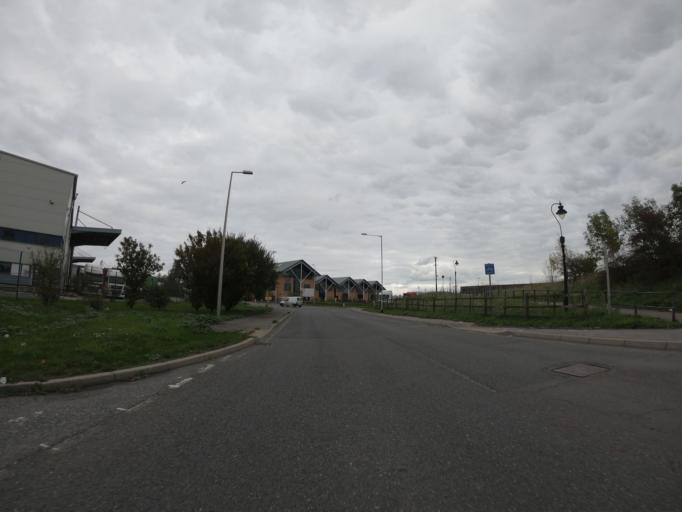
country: GB
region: England
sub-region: Borough of Thurrock
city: Tilbury
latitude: 51.4523
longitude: 0.3666
